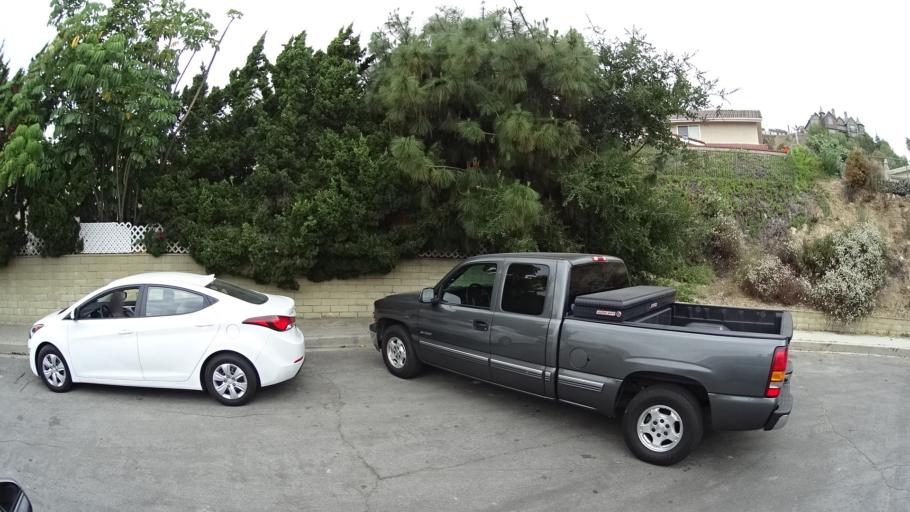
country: US
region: California
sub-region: Los Angeles County
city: Burbank
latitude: 34.2089
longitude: -118.3259
